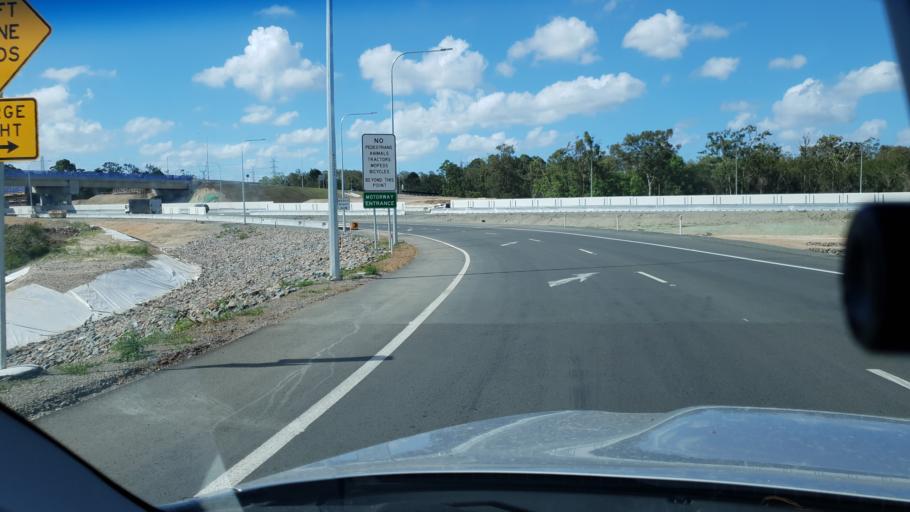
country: AU
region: Queensland
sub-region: Logan
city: Woodridge
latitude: -27.6542
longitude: 153.0712
